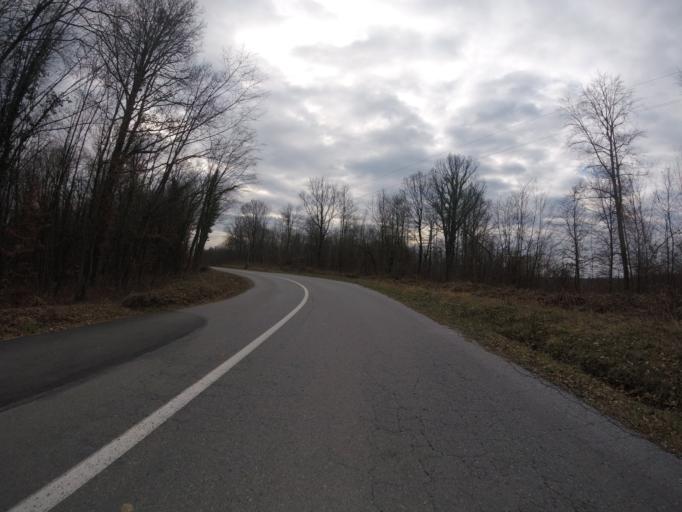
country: HR
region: Zagrebacka
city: Mraclin
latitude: 45.5453
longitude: 16.0569
